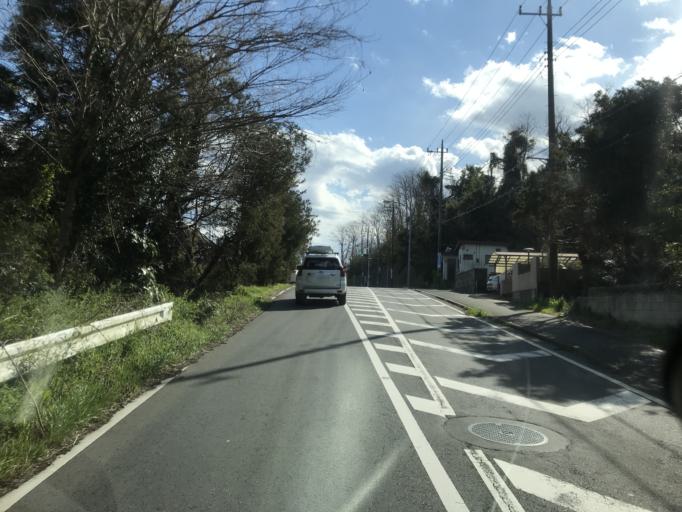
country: JP
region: Chiba
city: Katori-shi
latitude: 35.8903
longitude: 140.4127
